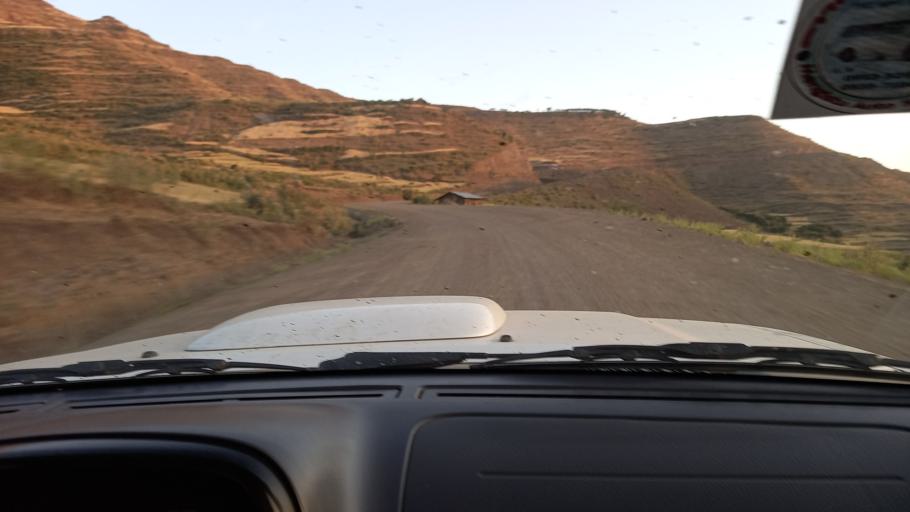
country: ET
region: Amhara
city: Debark'
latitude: 13.0537
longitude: 38.0188
